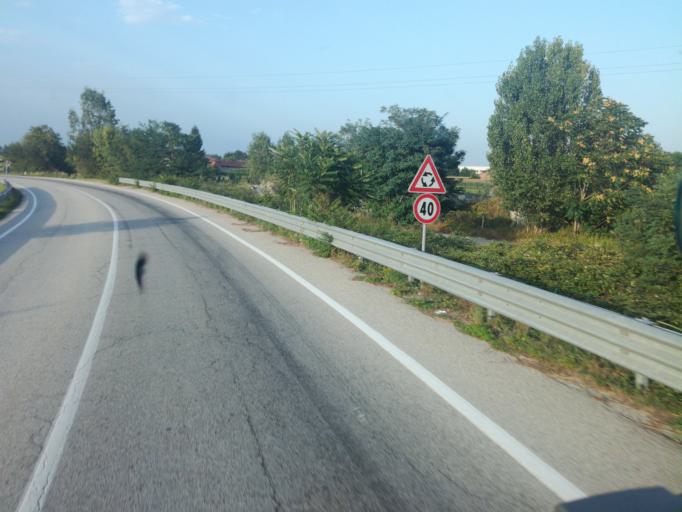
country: IT
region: Piedmont
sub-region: Provincia di Torino
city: Osasco
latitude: 44.8389
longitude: 7.3328
